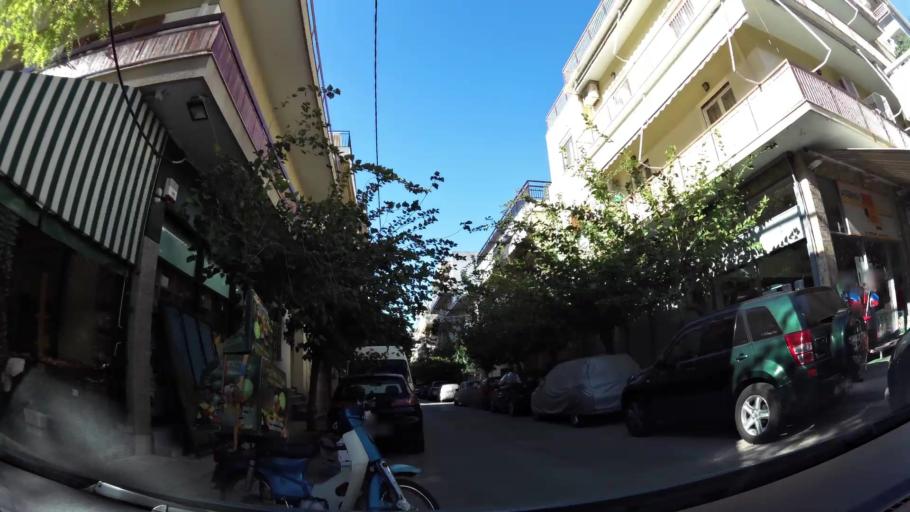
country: GR
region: Attica
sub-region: Nomarchia Athinas
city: Neo Psychiko
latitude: 37.9986
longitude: 23.7750
